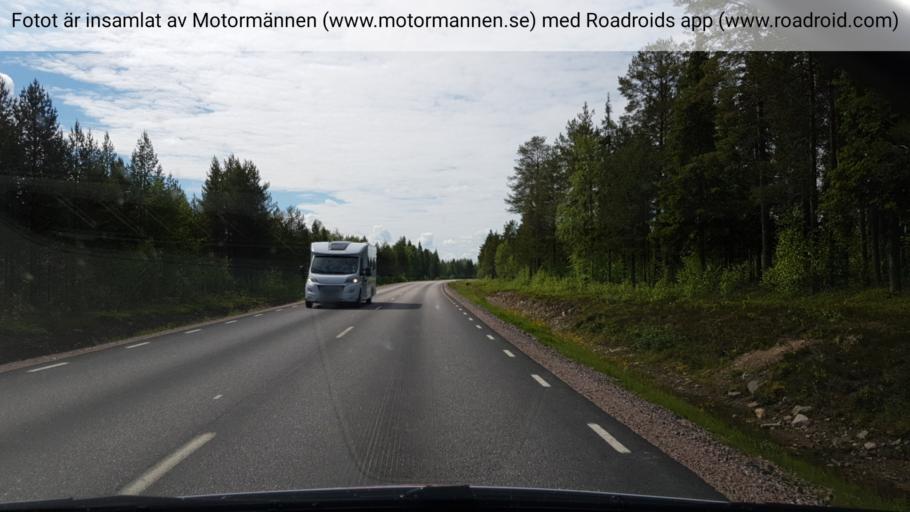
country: SE
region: Norrbotten
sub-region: Overtornea Kommun
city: OEvertornea
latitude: 66.4873
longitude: 23.7063
